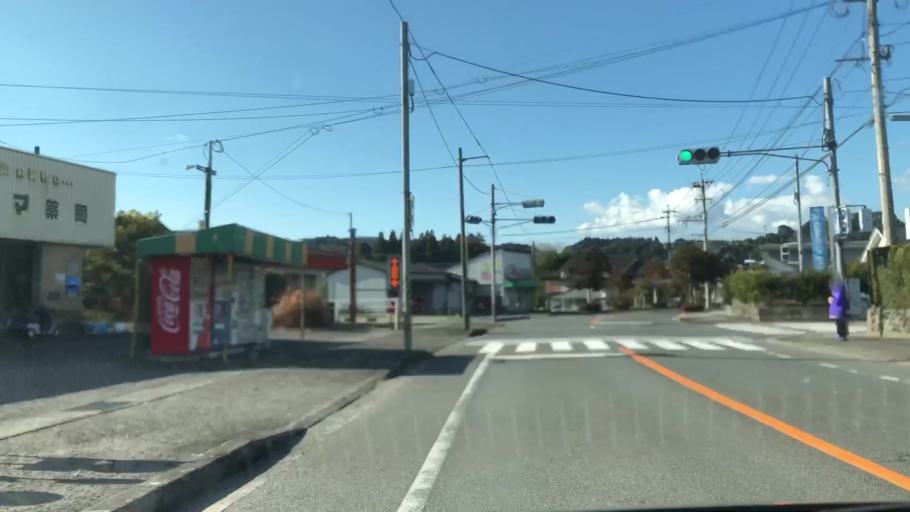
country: JP
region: Kagoshima
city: Satsumasendai
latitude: 31.8015
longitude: 130.4355
